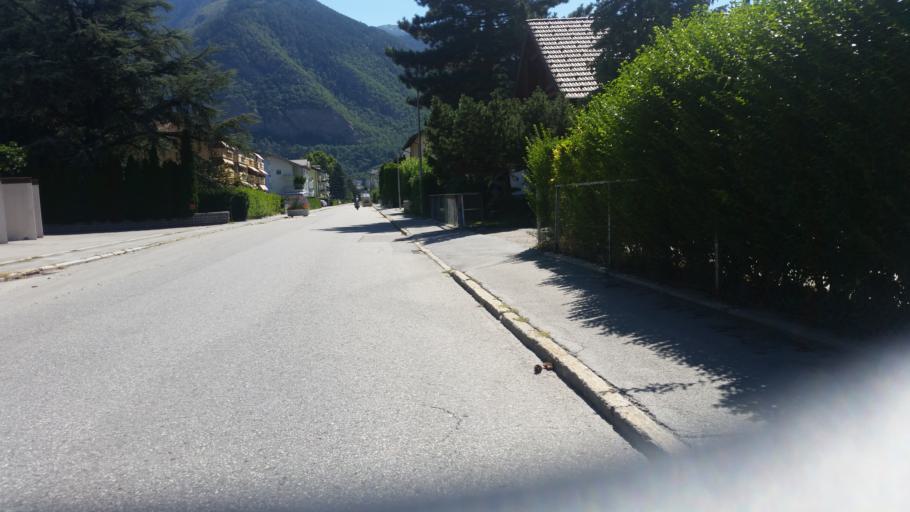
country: CH
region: Valais
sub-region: Visp District
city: Visp
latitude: 46.2996
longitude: 7.8753
